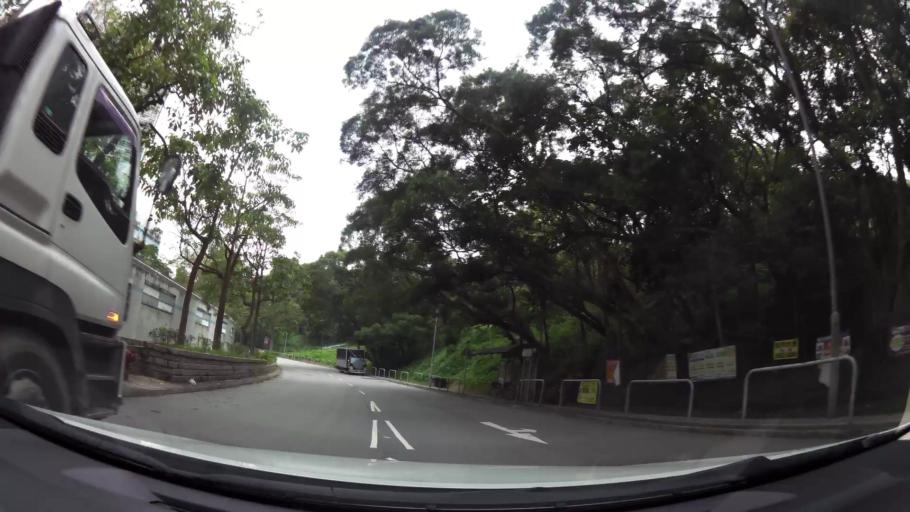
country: HK
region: Tai Po
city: Tai Po
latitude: 22.4613
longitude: 114.1719
